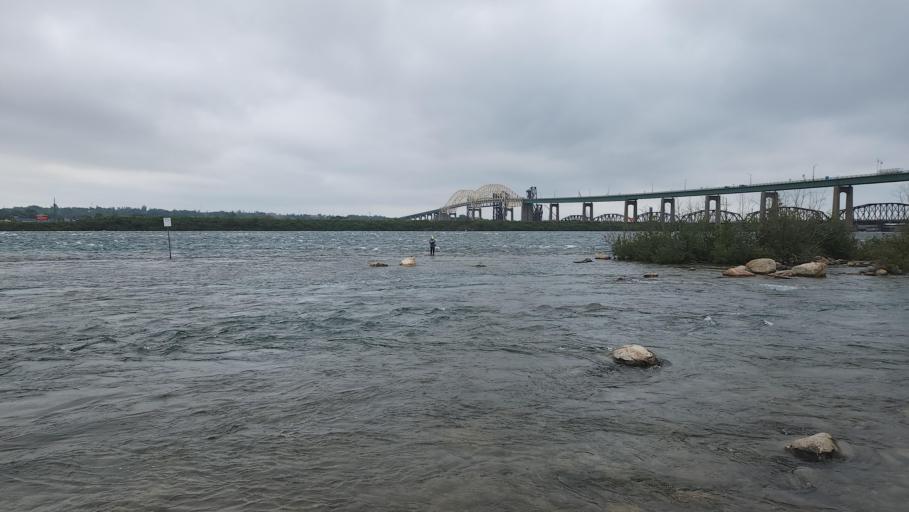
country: US
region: Michigan
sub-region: Chippewa County
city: Sault Ste. Marie
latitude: 46.5099
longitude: -84.3560
